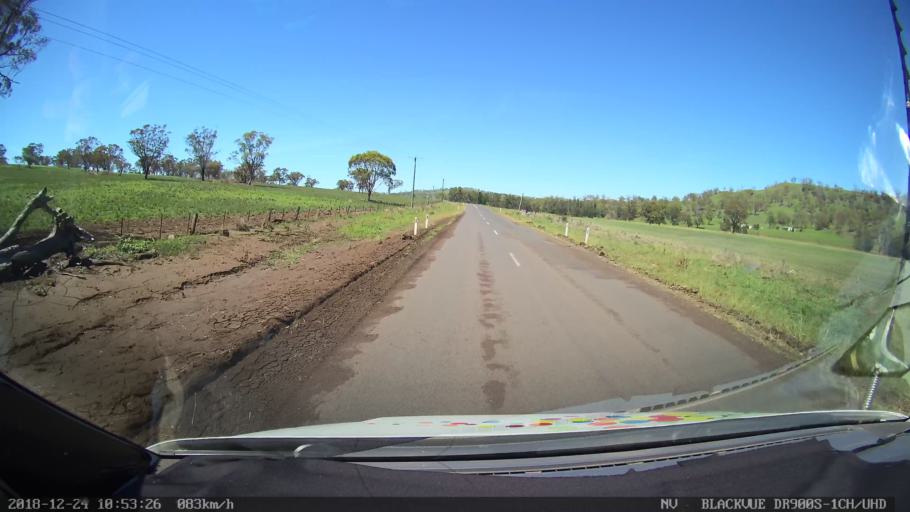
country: AU
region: New South Wales
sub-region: Upper Hunter Shire
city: Merriwa
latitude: -31.9915
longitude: 150.4210
